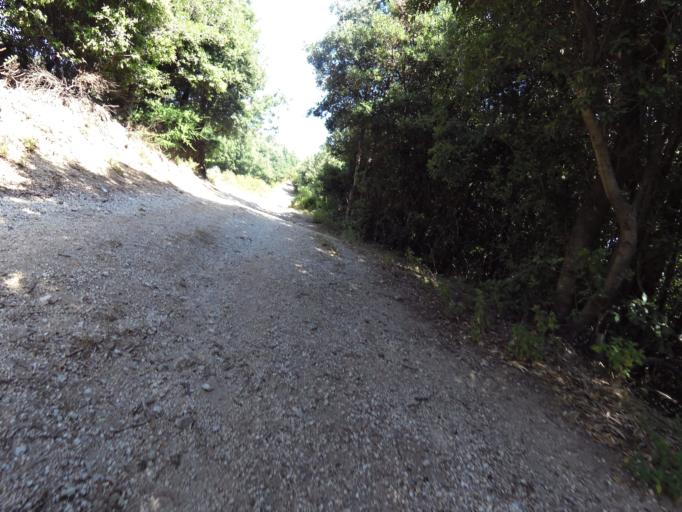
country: IT
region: Calabria
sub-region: Provincia di Reggio Calabria
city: Bivongi
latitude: 38.5045
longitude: 16.4387
